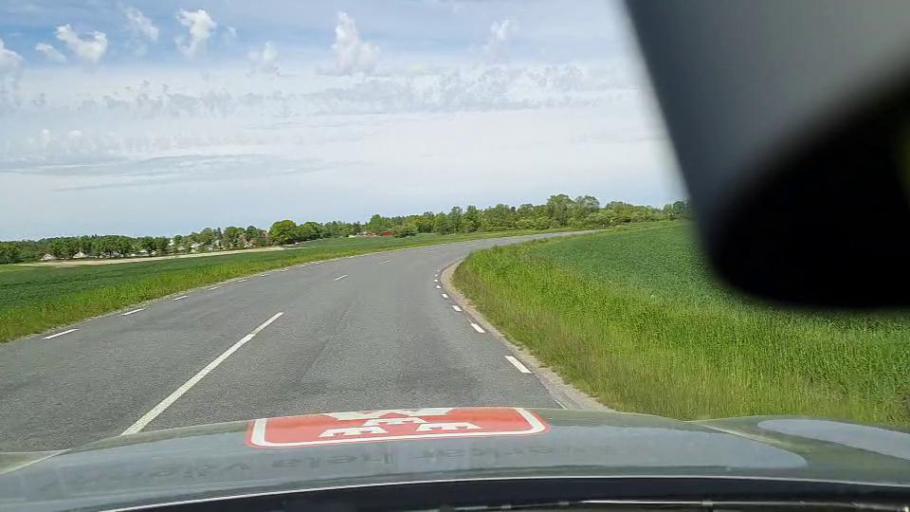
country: SE
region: Soedermanland
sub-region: Eskilstuna Kommun
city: Skogstorp
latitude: 59.3101
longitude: 16.4633
